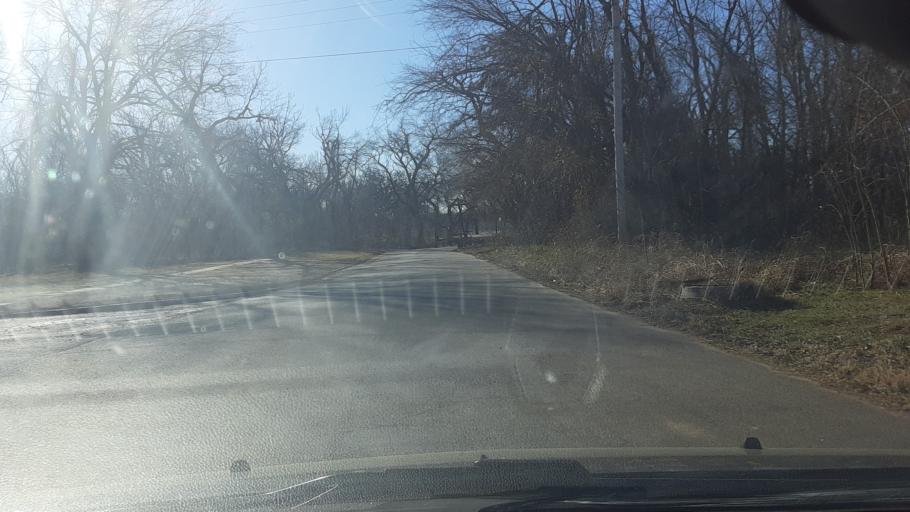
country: US
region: Oklahoma
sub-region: Logan County
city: Guthrie
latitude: 35.8719
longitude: -97.4276
